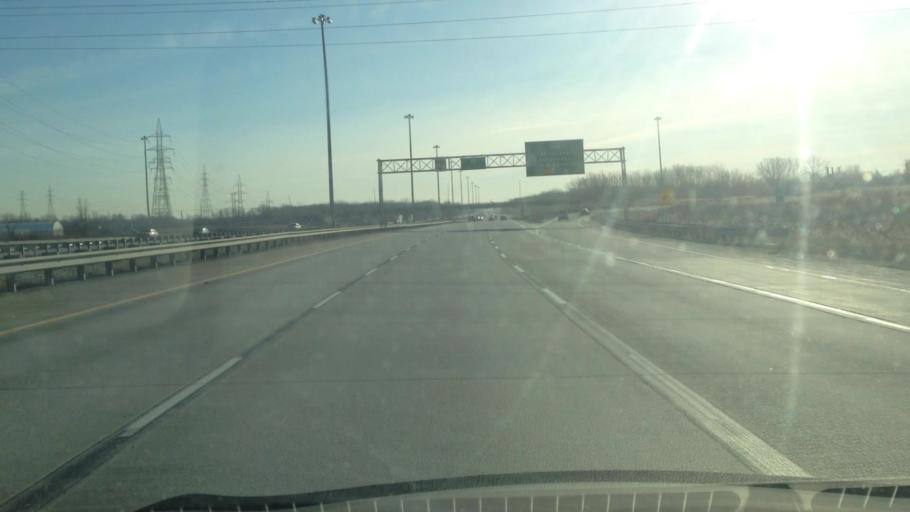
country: CA
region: Quebec
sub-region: Laurentides
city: Boisbriand
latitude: 45.5927
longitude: -73.8509
